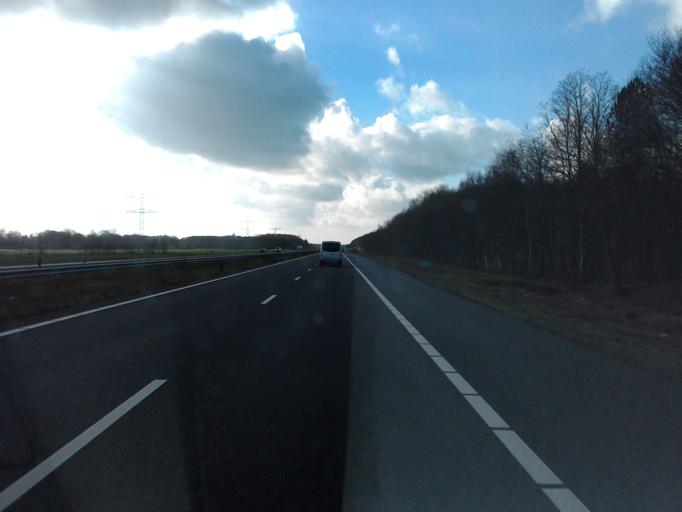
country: NL
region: North Brabant
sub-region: Gemeente Eersel
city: Eersel
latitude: 51.3793
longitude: 5.3392
